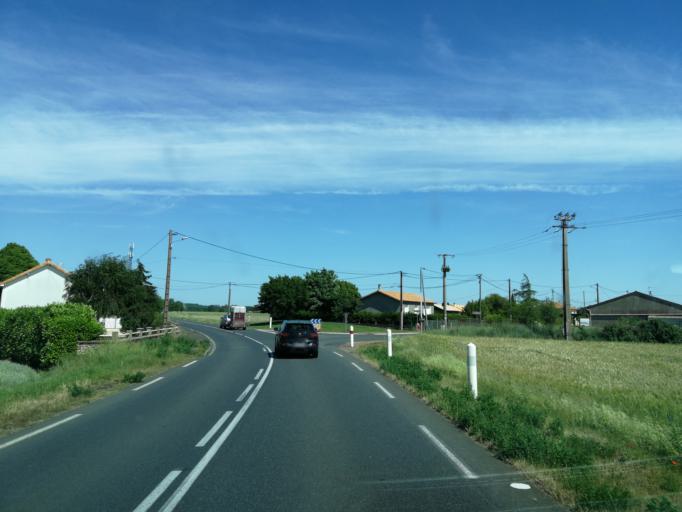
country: FR
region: Poitou-Charentes
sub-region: Departement des Deux-Sevres
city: Saint-Leger-de-Montbrun
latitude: 46.9757
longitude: -0.0556
